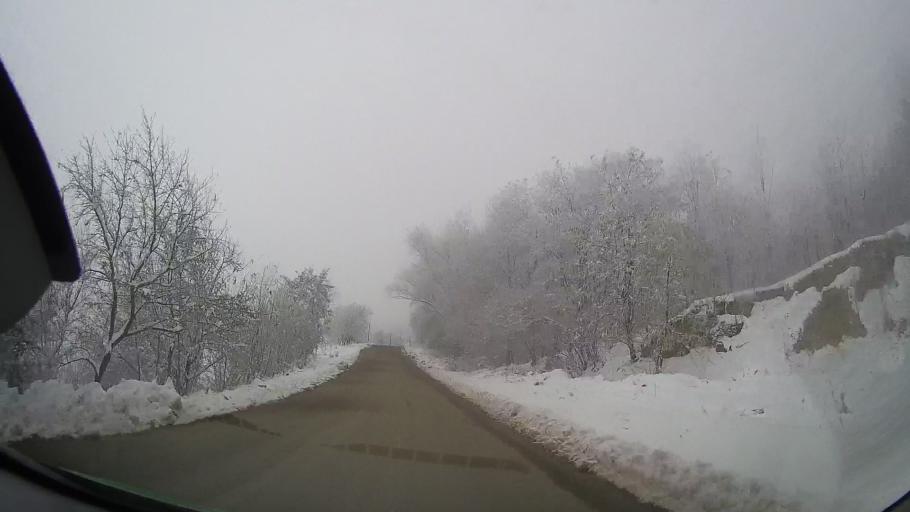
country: RO
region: Iasi
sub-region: Comuna Tansa
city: Suhulet
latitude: 46.9006
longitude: 27.2421
